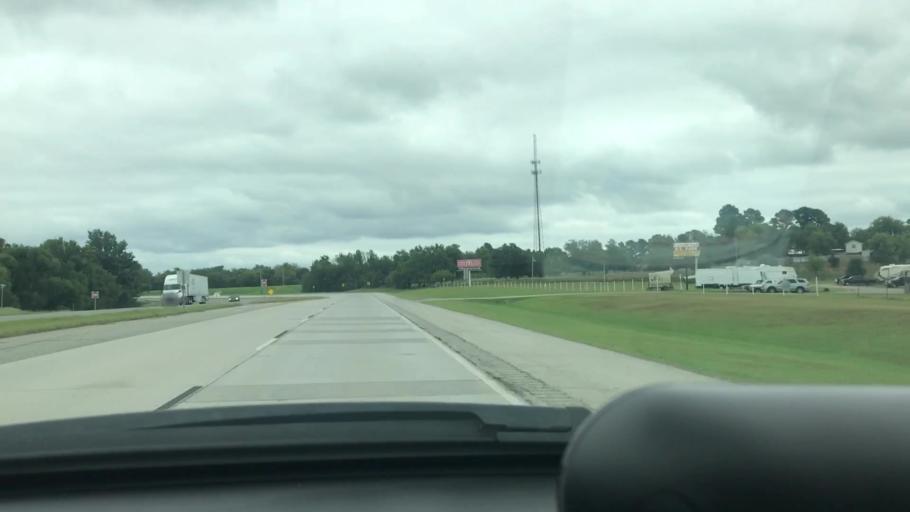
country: US
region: Oklahoma
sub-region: Wagoner County
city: Wagoner
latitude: 35.9137
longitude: -95.3995
